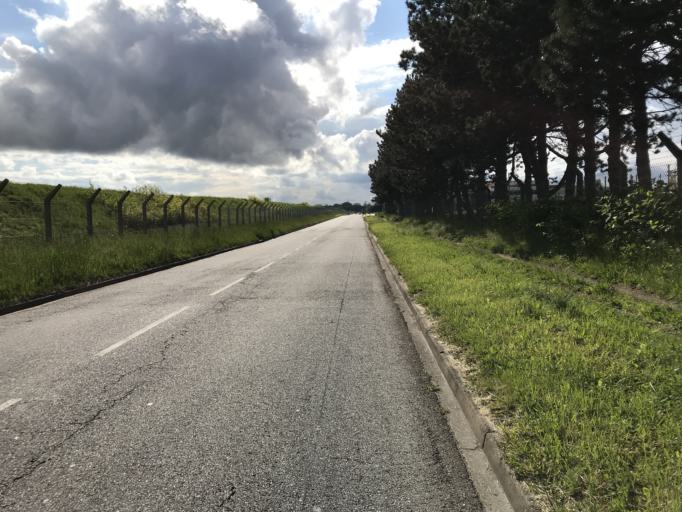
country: FR
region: Ile-de-France
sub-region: Departement des Yvelines
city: Velizy-Villacoublay
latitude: 48.7771
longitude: 2.2005
